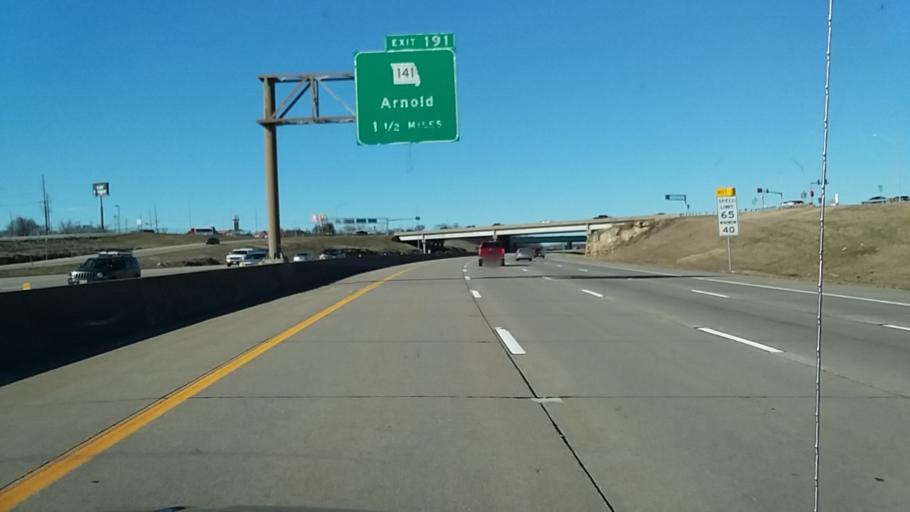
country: US
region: Missouri
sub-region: Jefferson County
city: Arnold
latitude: 38.4133
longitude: -90.3892
